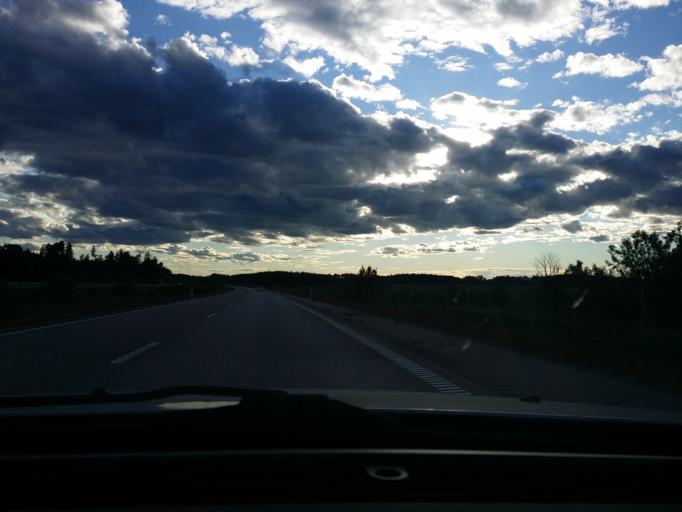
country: SE
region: Uppsala
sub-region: Enkopings Kommun
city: Grillby
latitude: 59.6394
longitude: 17.2552
